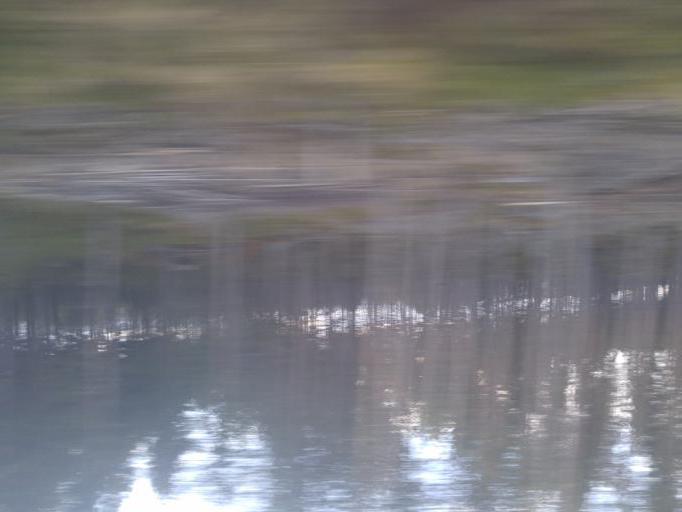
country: NO
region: Oppland
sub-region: Dovre
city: Dovre
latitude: 61.9501
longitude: 9.2834
